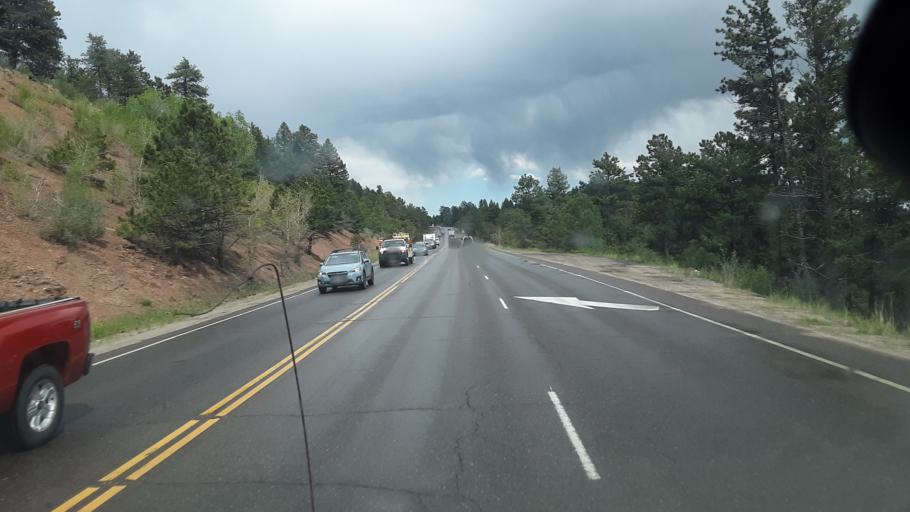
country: US
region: Colorado
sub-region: Jefferson County
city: Evergreen
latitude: 39.4533
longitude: -105.4317
